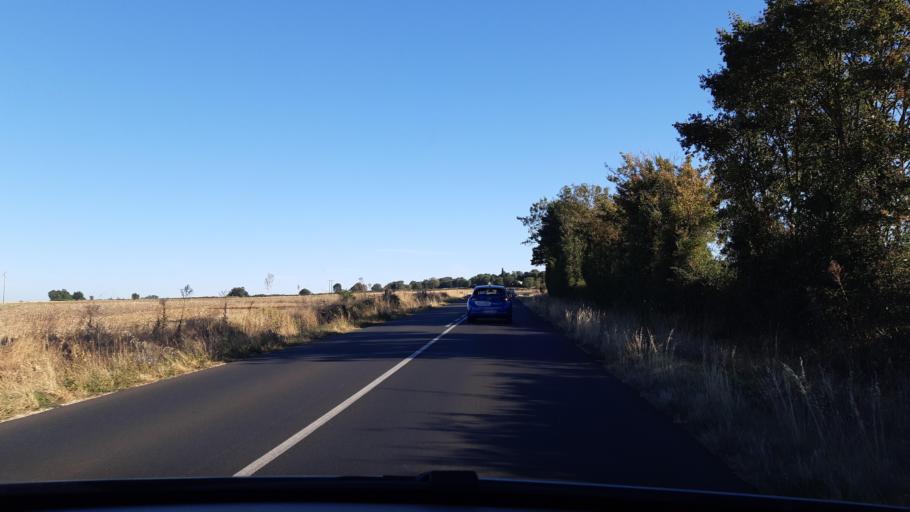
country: FR
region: Poitou-Charentes
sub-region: Departement des Deux-Sevres
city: Exireuil
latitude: 46.4317
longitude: -0.2034
